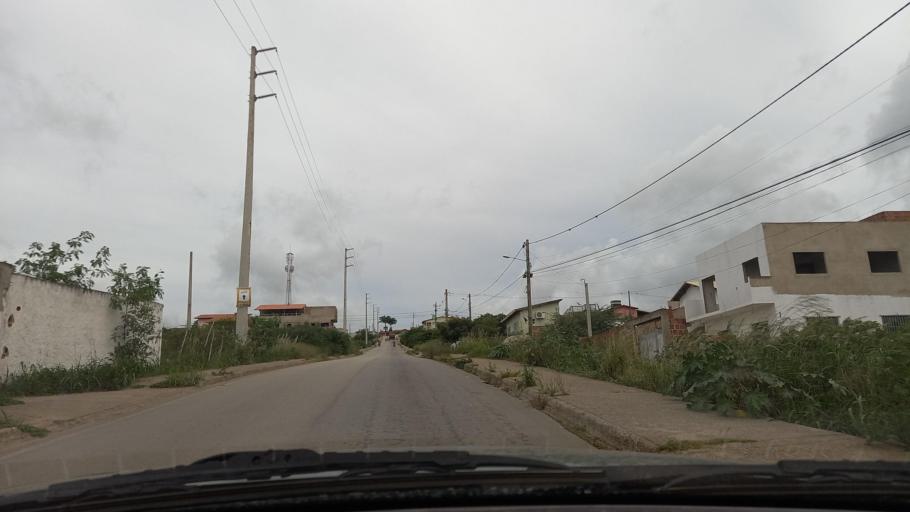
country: BR
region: Pernambuco
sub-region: Gravata
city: Gravata
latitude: -8.2095
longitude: -35.5794
